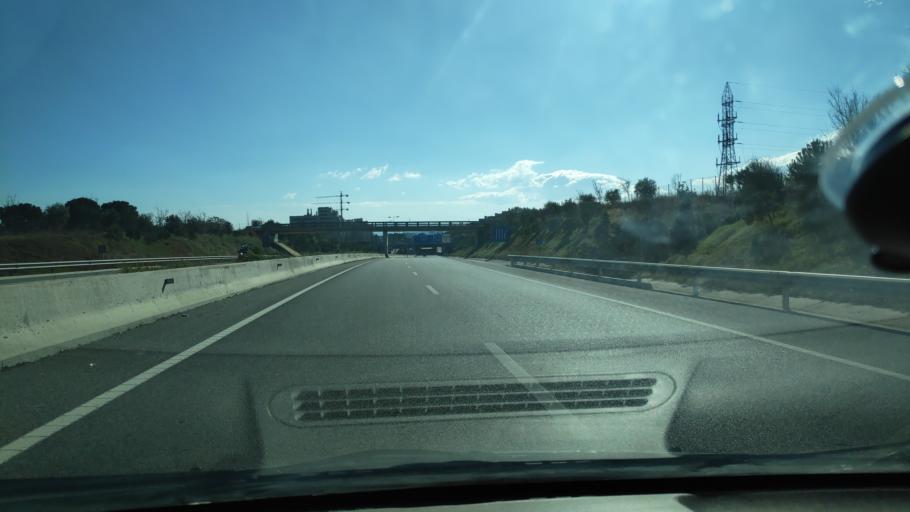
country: ES
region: Catalonia
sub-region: Provincia de Barcelona
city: Sant Quirze del Valles
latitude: 41.5676
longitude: 2.0763
